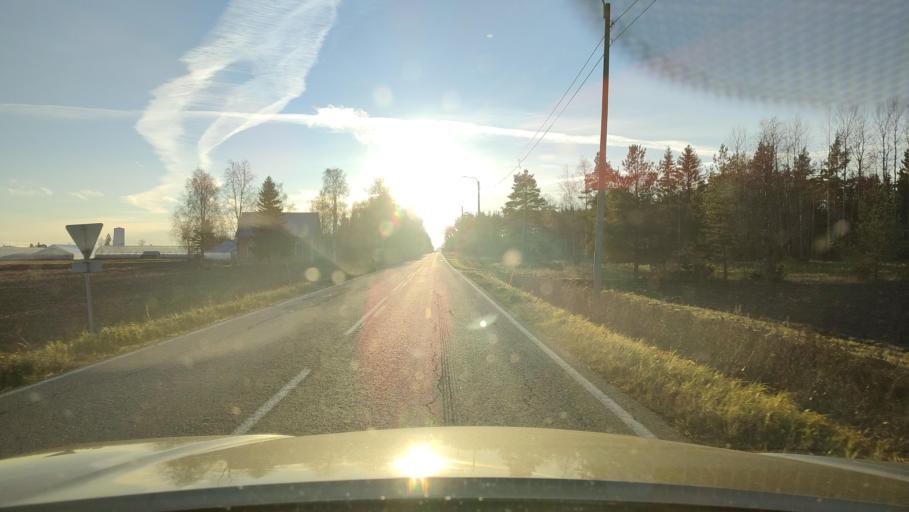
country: FI
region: Ostrobothnia
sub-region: Vaasa
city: Malax
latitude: 62.7079
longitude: 21.6047
